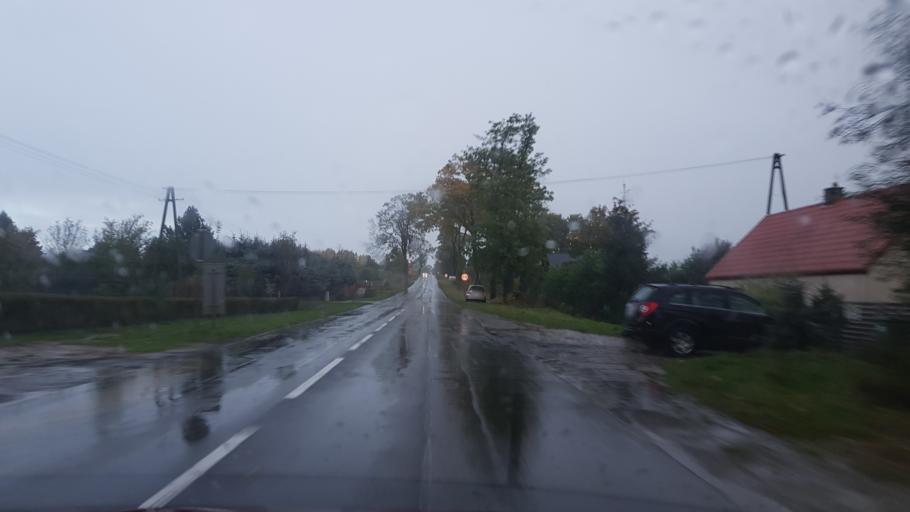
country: PL
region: Greater Poland Voivodeship
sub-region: Powiat pilski
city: Szydlowo
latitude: 53.1614
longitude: 16.6241
